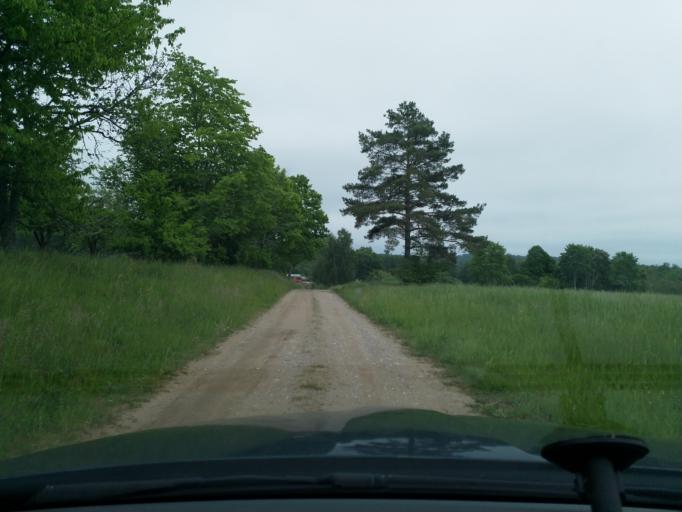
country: LV
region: Kuldigas Rajons
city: Kuldiga
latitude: 56.8780
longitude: 21.8253
